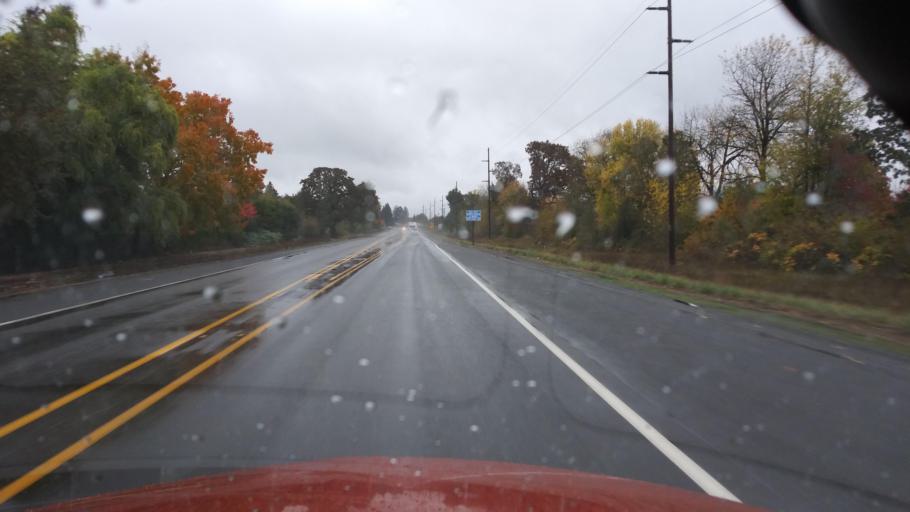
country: US
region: Oregon
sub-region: Washington County
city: Forest Grove
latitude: 45.5102
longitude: -123.0969
